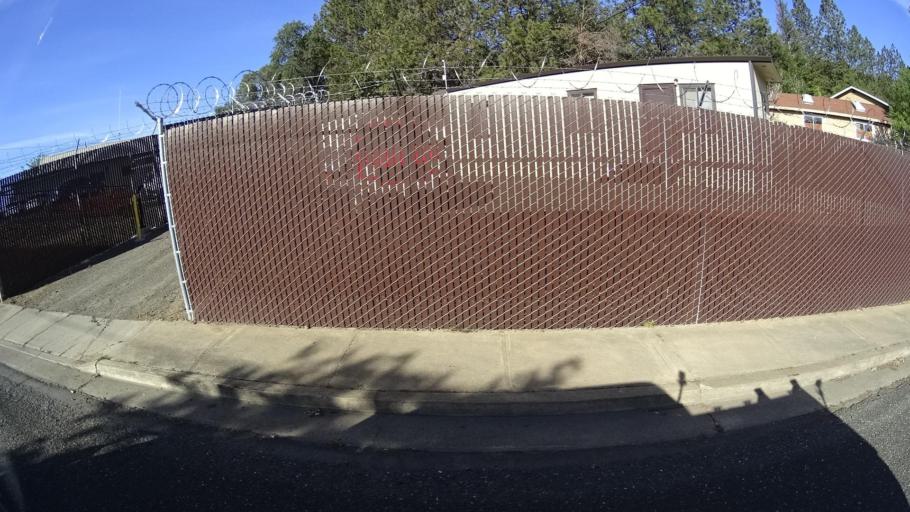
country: US
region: California
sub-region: Lake County
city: Lakeport
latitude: 39.0416
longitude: -122.9275
